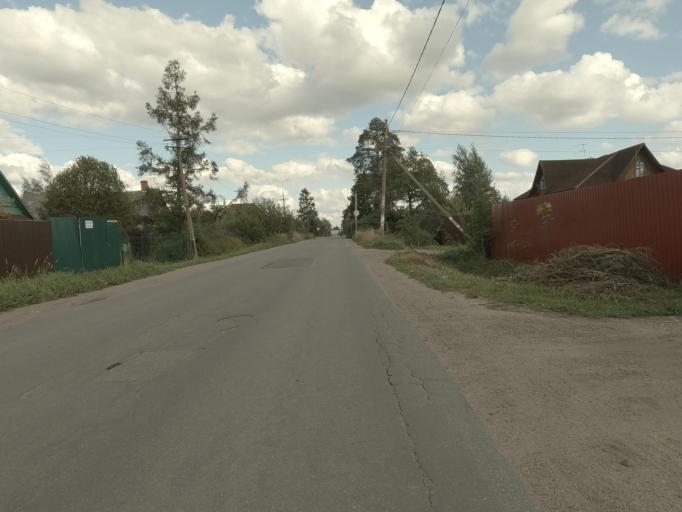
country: RU
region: Leningrad
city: Ul'yanovka
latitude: 59.6336
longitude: 30.7759
